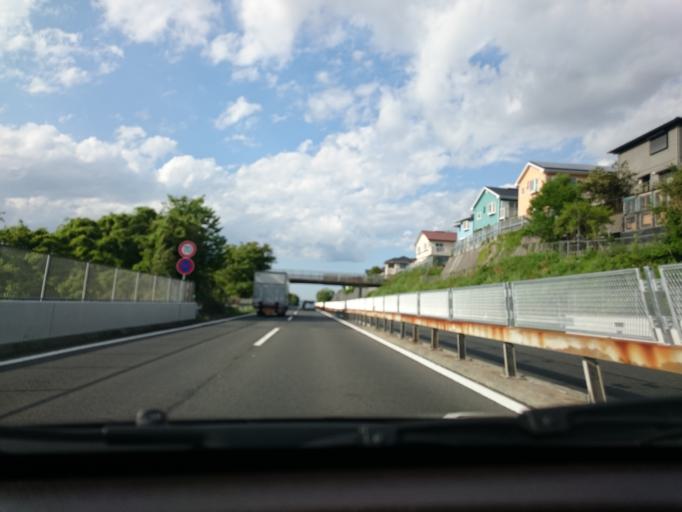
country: JP
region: Kanagawa
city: Oiso
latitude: 35.3409
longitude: 139.2963
